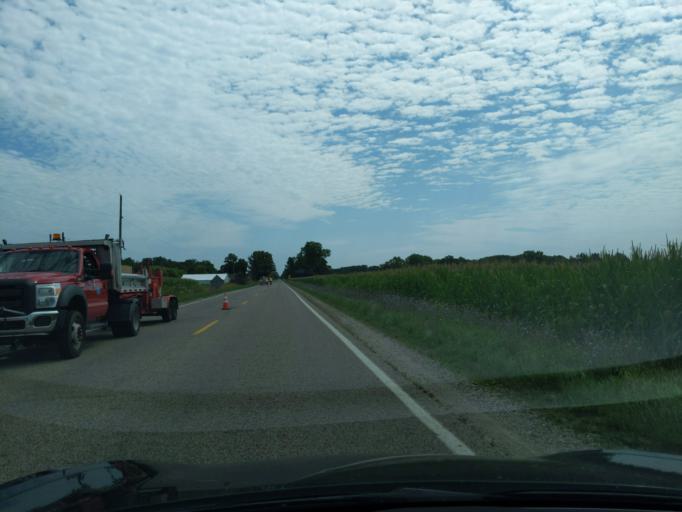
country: US
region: Michigan
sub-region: Gratiot County
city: Breckenridge
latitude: 43.2919
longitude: -84.4341
